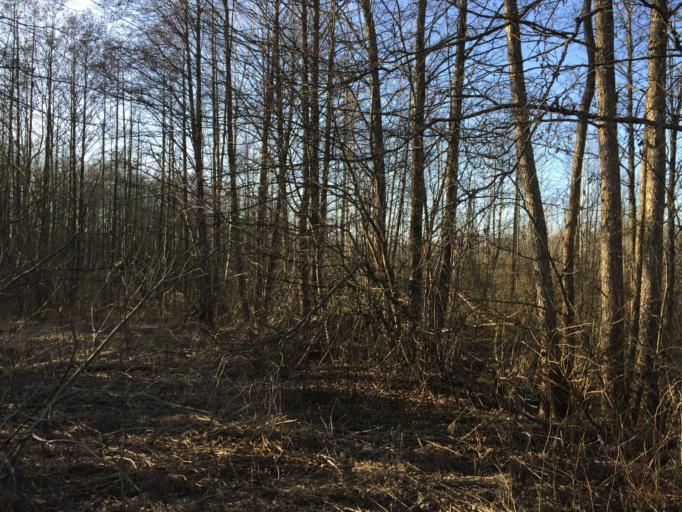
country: LV
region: Riga
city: Bergi
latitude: 56.9804
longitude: 24.2601
